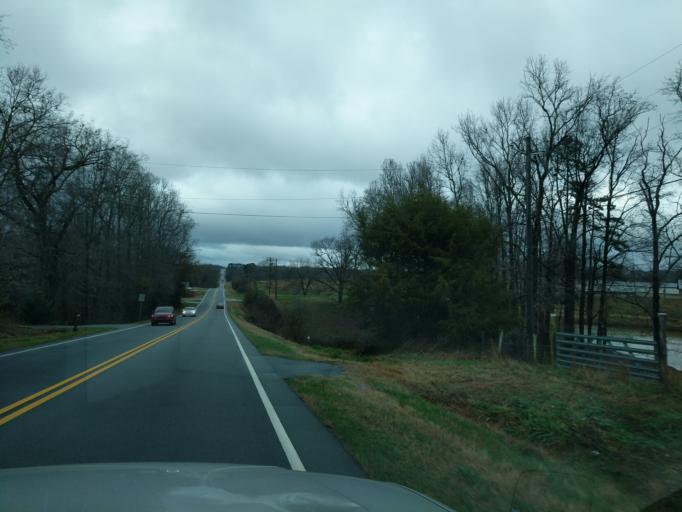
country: US
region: Georgia
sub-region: Franklin County
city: Lavonia
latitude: 34.3773
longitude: -83.0866
